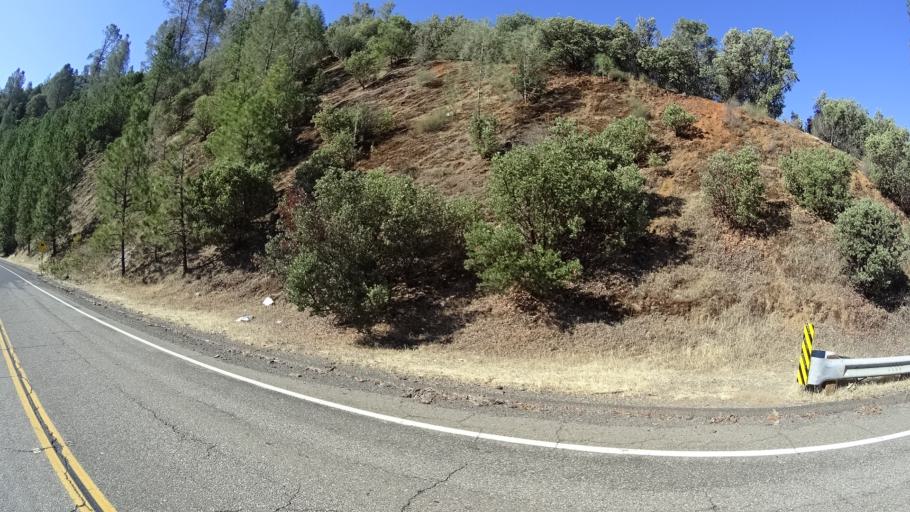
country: US
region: California
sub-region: Tuolumne County
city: Columbia
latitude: 38.0367
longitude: -120.4521
